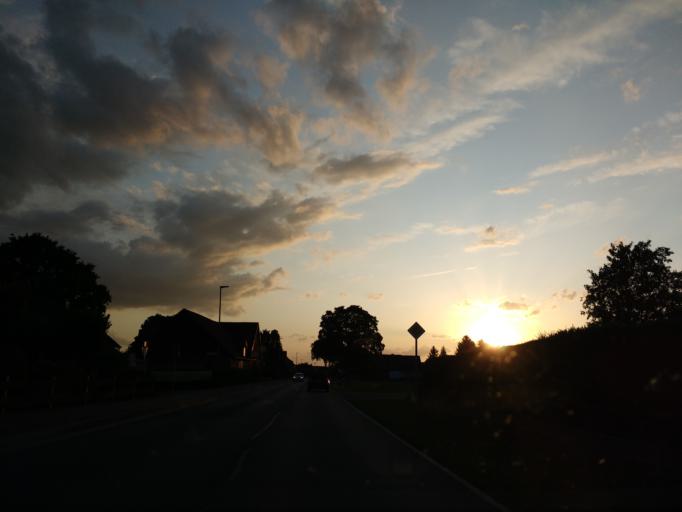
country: DE
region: Lower Saxony
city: Rehburg-Loccum
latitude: 52.4793
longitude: 9.2340
